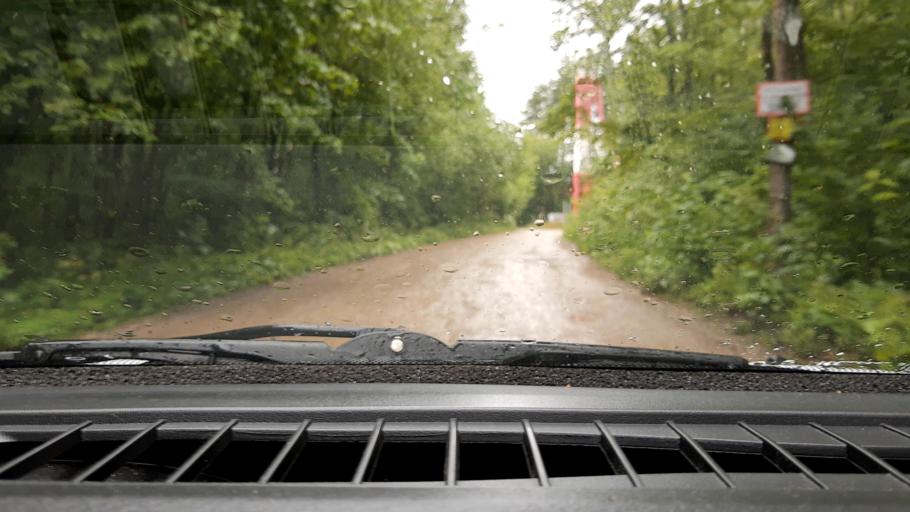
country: RU
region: Nizjnij Novgorod
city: Babino
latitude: 56.1456
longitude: 43.6411
